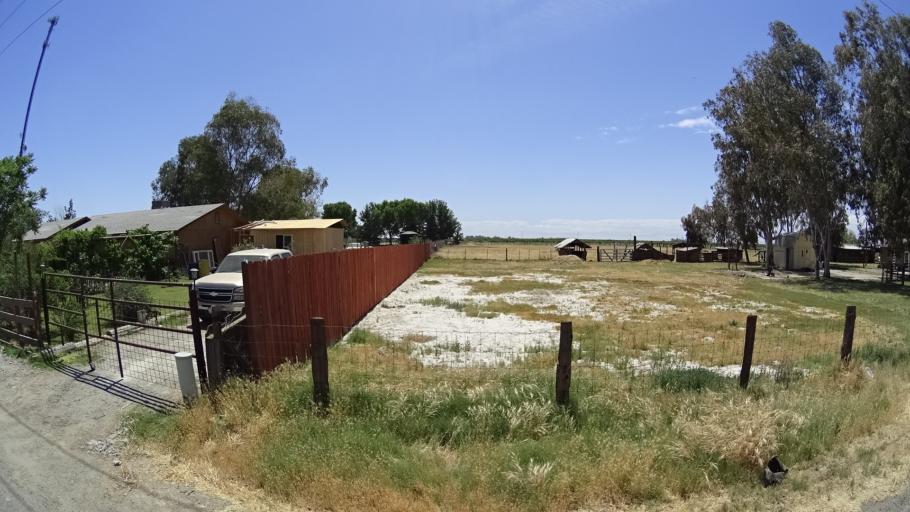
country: US
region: California
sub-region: Kings County
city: Stratford
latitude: 36.2330
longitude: -119.7905
